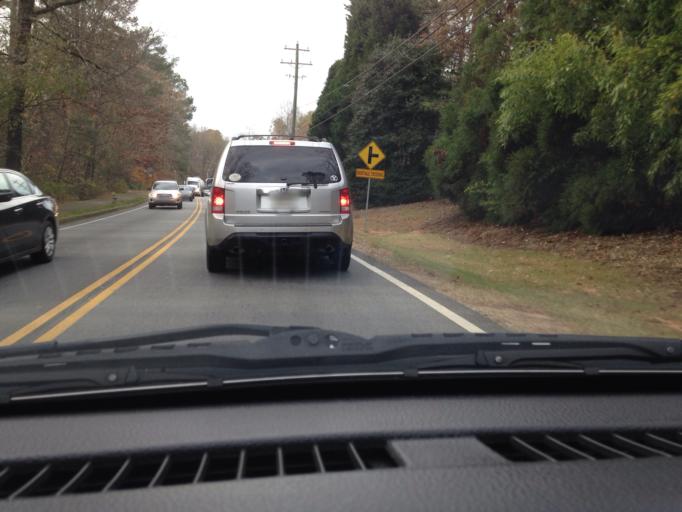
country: US
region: Georgia
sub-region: Fulton County
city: Johns Creek
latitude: 34.0868
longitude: -84.1915
